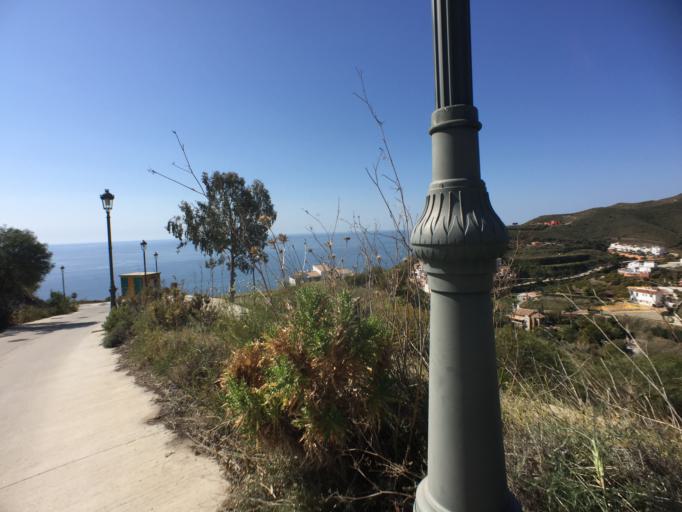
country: ES
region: Andalusia
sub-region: Provincia de Malaga
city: Nerja
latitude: 36.7463
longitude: -3.9092
